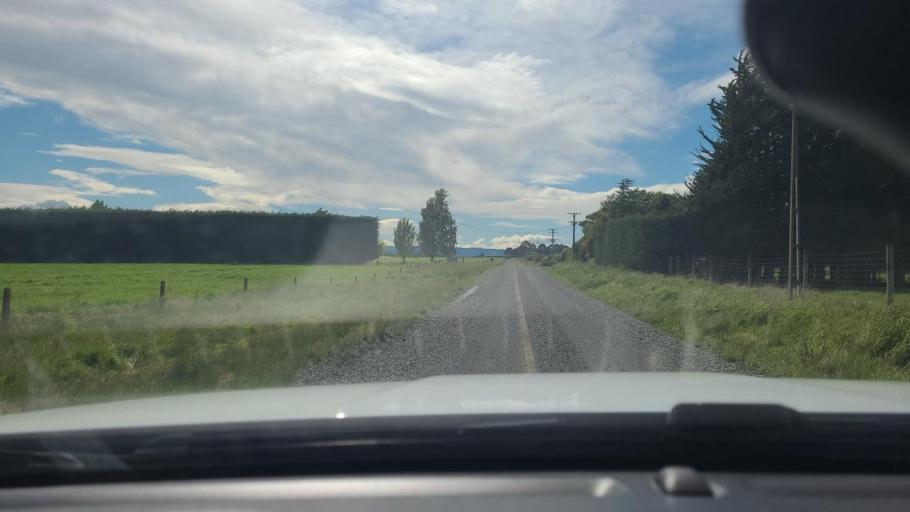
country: NZ
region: Southland
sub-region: Southland District
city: Winton
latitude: -46.0294
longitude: 168.1804
